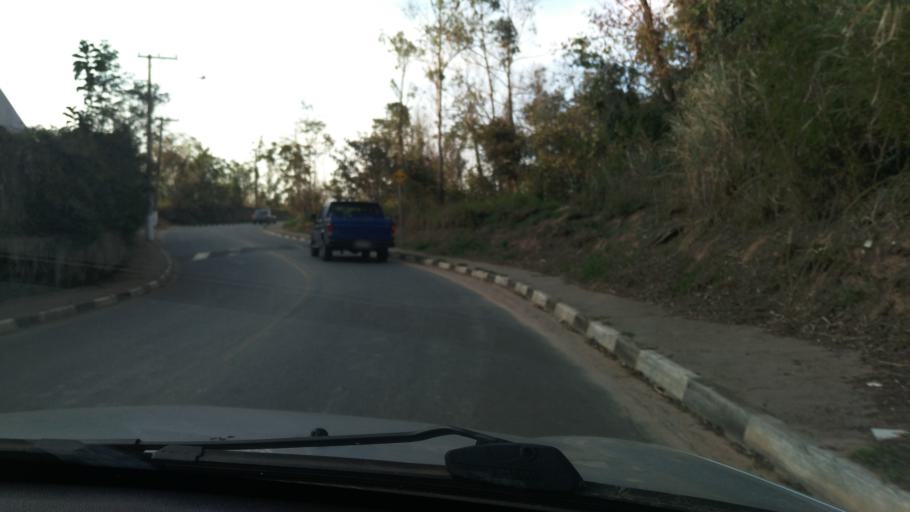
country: BR
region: Sao Paulo
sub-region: Vinhedo
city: Vinhedo
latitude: -23.0293
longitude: -47.0060
